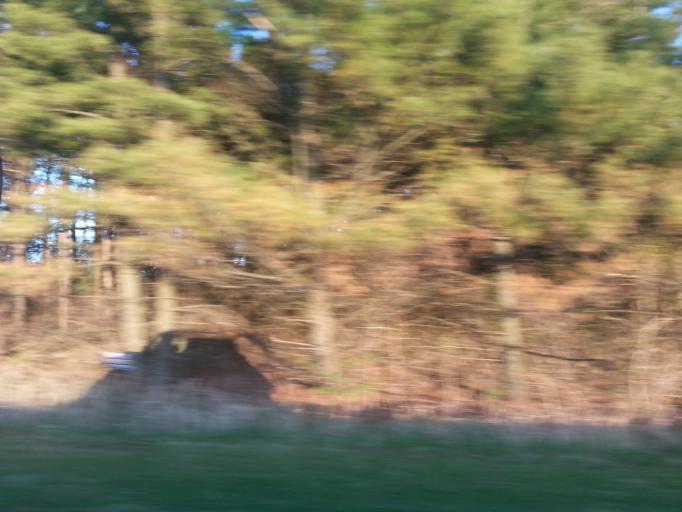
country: US
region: Wisconsin
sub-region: Pierce County
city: Prescott
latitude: 44.8126
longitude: -92.8034
